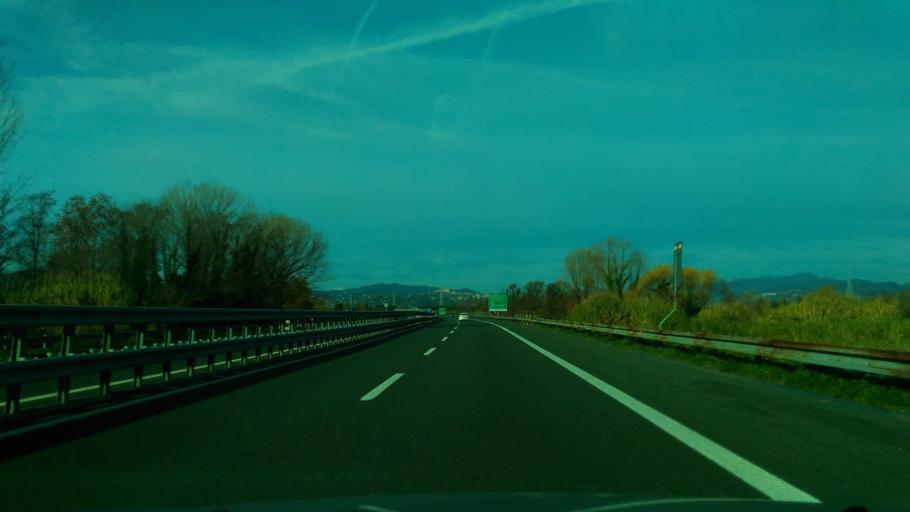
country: IT
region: Liguria
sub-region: Provincia di La Spezia
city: Sarzana
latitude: 44.0952
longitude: 9.9646
